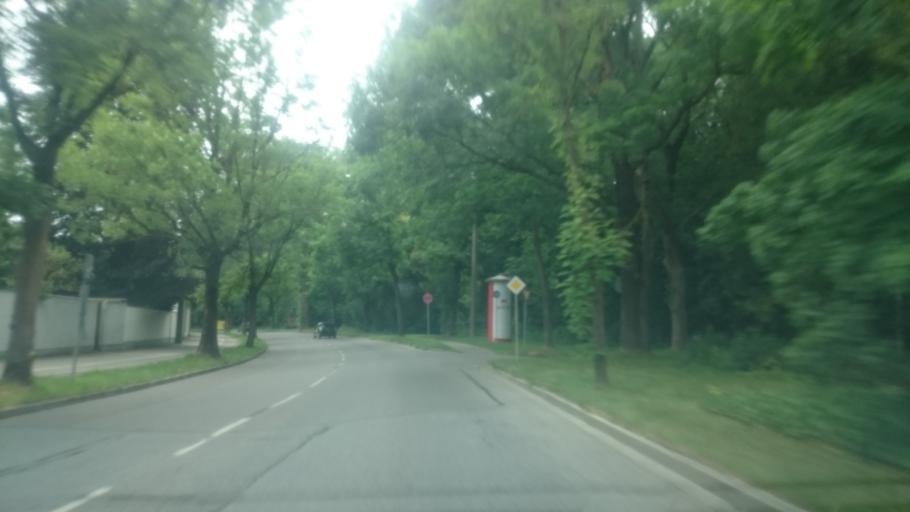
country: DE
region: Bavaria
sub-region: Swabia
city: Augsburg
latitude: 48.3560
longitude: 10.9350
